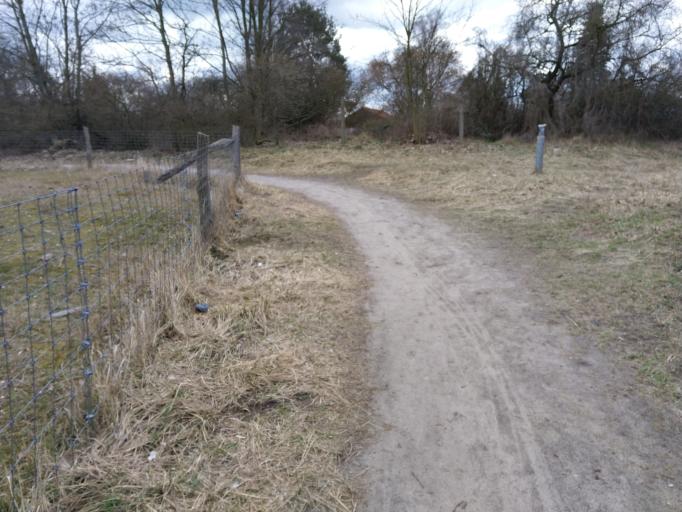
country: DE
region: Berlin
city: Karlshorst
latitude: 52.4889
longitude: 13.5436
